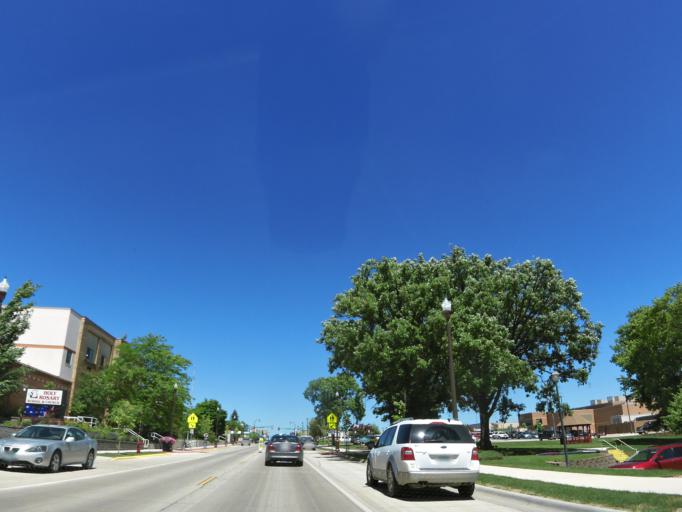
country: US
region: Minnesota
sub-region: Becker County
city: Detroit Lakes
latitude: 46.8139
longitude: -95.8455
